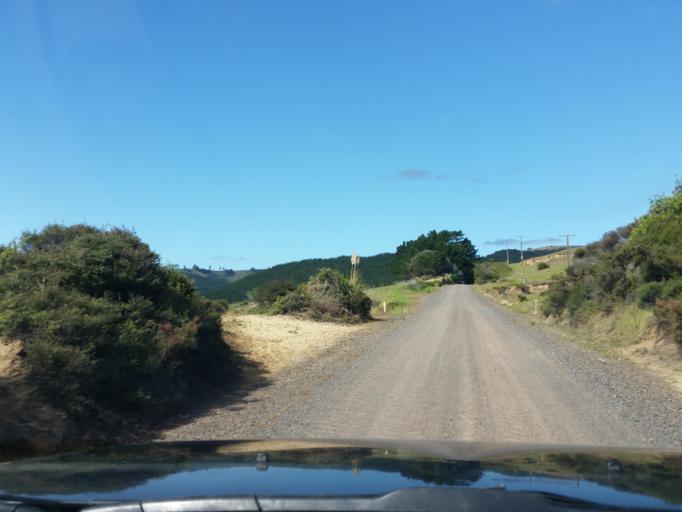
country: NZ
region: Northland
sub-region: Kaipara District
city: Dargaville
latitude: -35.7042
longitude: 173.5321
